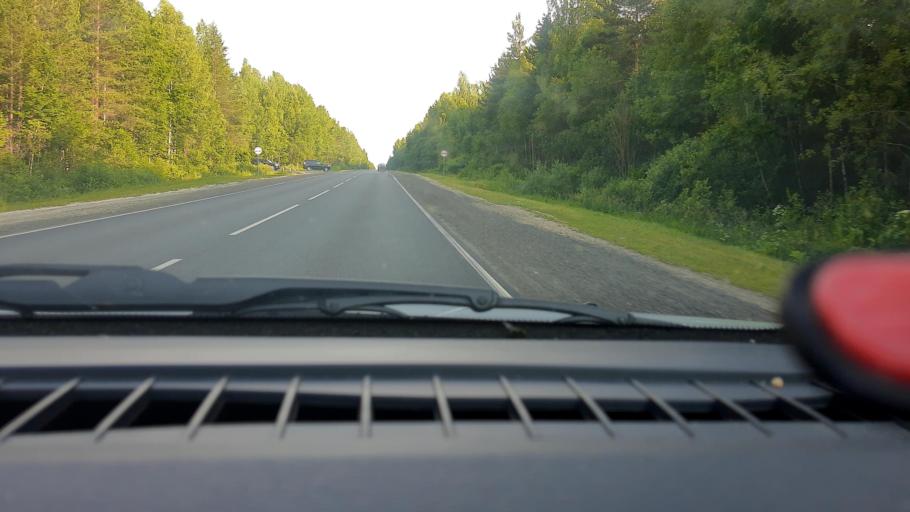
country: RU
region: Nizjnij Novgorod
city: Arzamas
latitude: 55.4394
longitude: 43.8936
